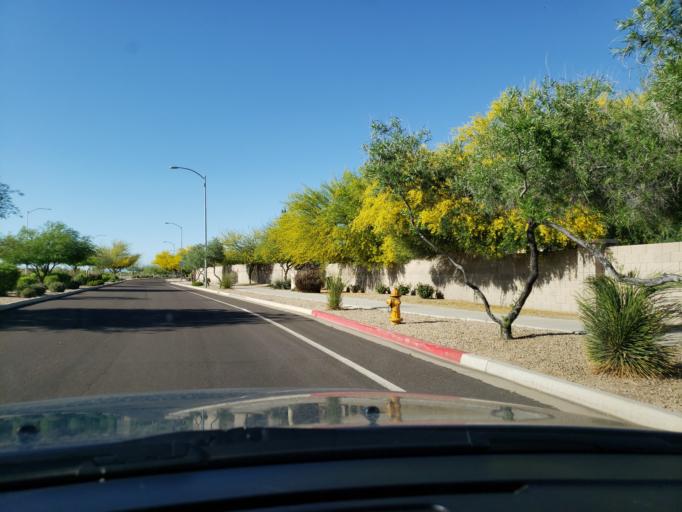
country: US
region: Arizona
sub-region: Maricopa County
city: Youngtown
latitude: 33.5722
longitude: -112.3111
